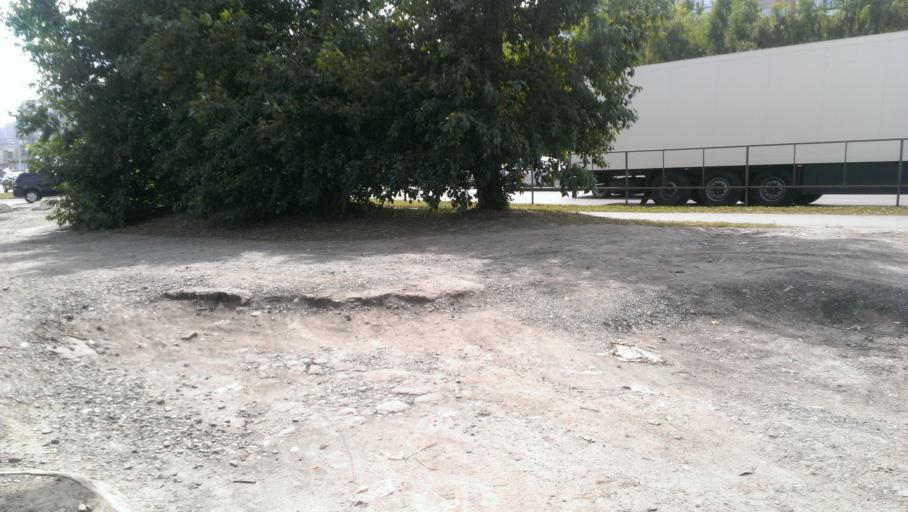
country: RU
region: Altai Krai
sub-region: Gorod Barnaulskiy
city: Barnaul
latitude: 53.3464
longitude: 83.6970
